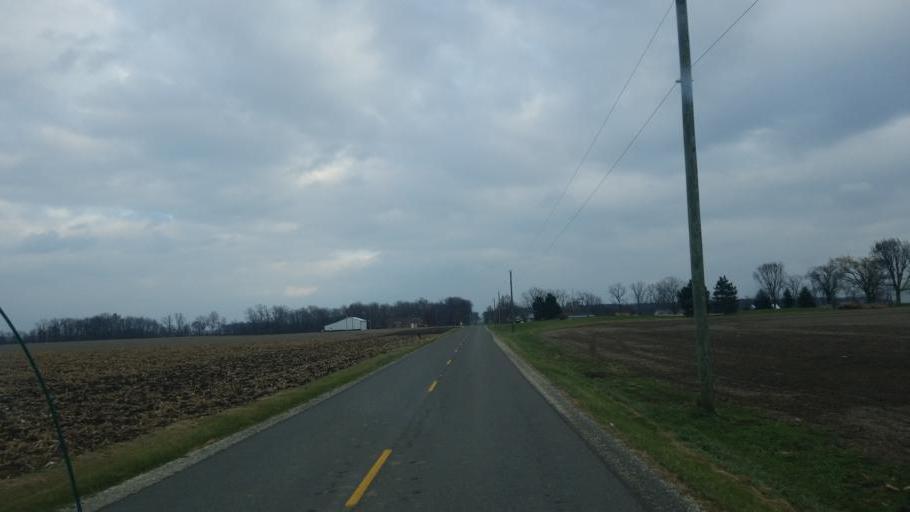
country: US
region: Ohio
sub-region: Mercer County
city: Coldwater
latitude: 40.5089
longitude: -84.6615
